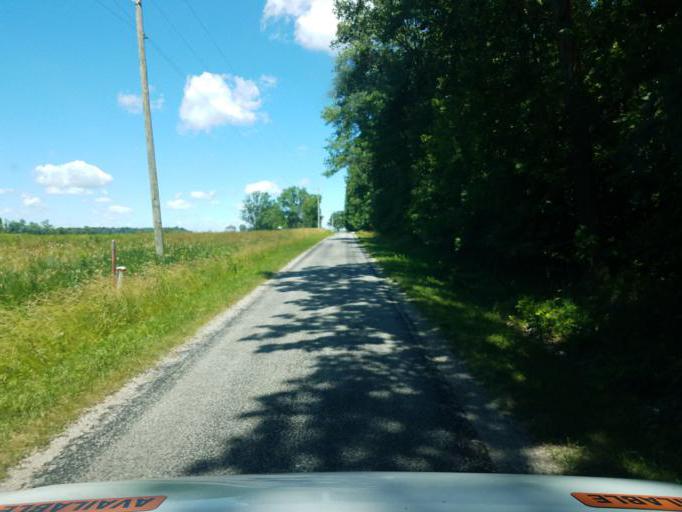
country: US
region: Ohio
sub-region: Crawford County
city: Bucyrus
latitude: 40.7288
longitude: -82.9201
